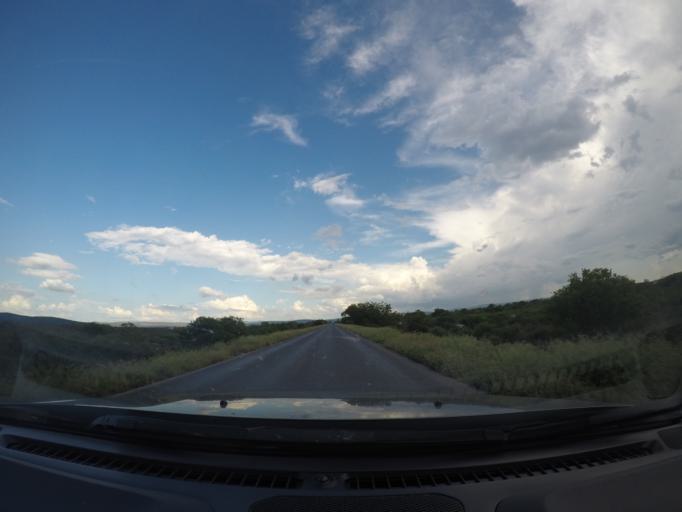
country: BR
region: Bahia
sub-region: Ibotirama
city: Ibotirama
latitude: -12.1583
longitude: -43.2974
